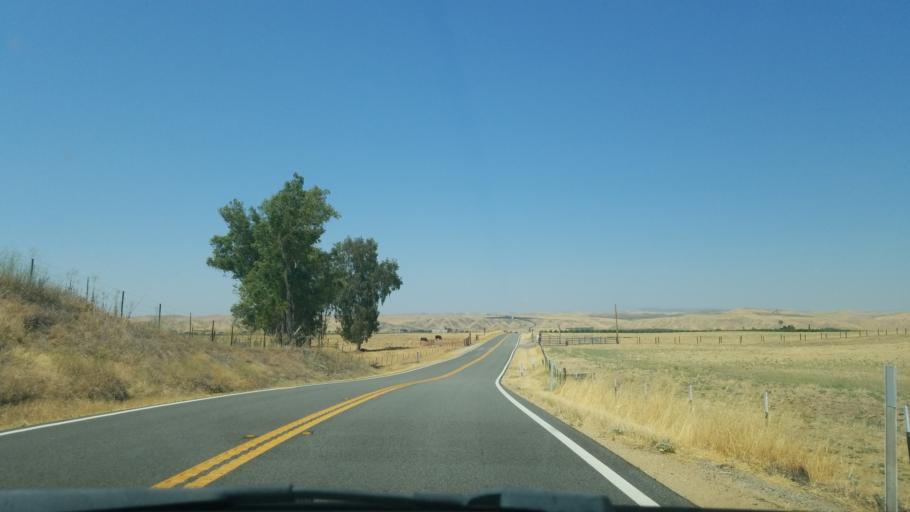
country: US
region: California
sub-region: San Luis Obispo County
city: Shandon
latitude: 35.6217
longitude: -120.3997
